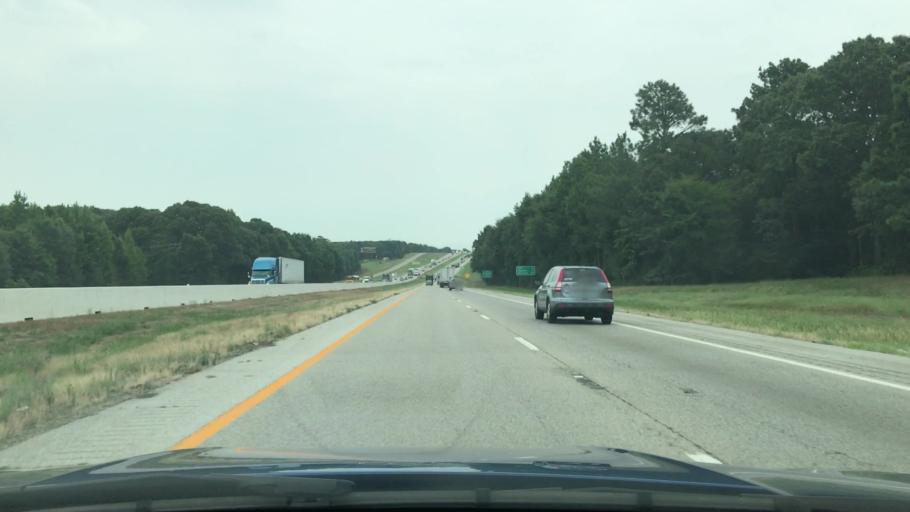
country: US
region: Texas
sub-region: Van Zandt County
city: Van
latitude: 32.4962
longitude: -95.5731
